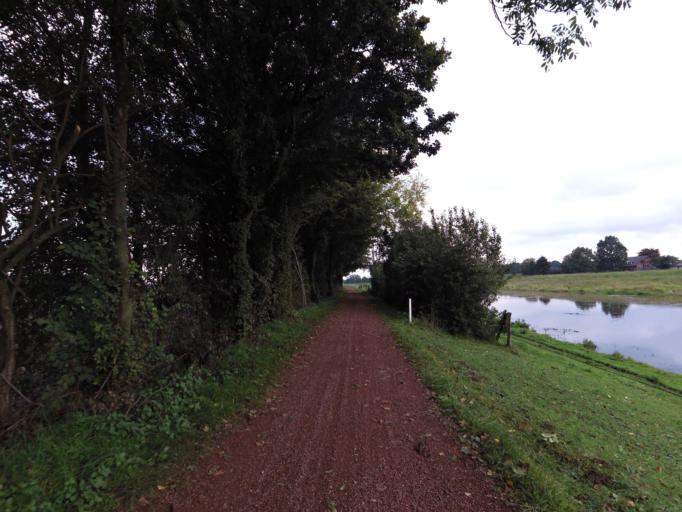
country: DE
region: North Rhine-Westphalia
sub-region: Regierungsbezirk Munster
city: Isselburg
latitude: 51.8486
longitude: 6.5276
